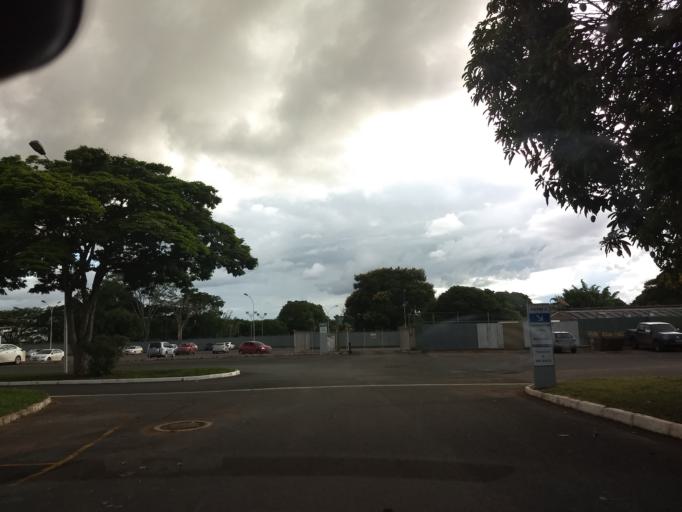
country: BR
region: Federal District
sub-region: Brasilia
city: Brasilia
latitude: -15.8103
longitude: -47.9609
